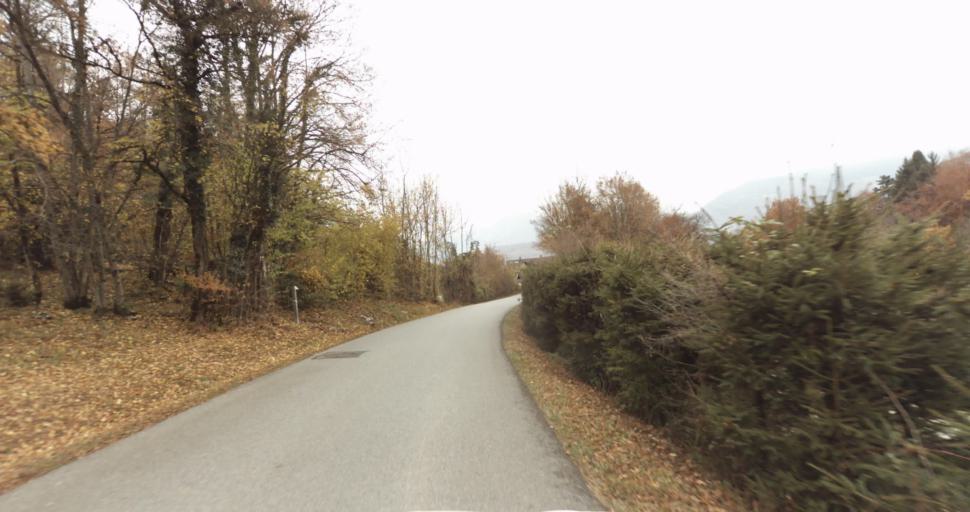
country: FR
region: Rhone-Alpes
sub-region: Departement de la Haute-Savoie
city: Talloires
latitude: 45.8184
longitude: 6.1966
